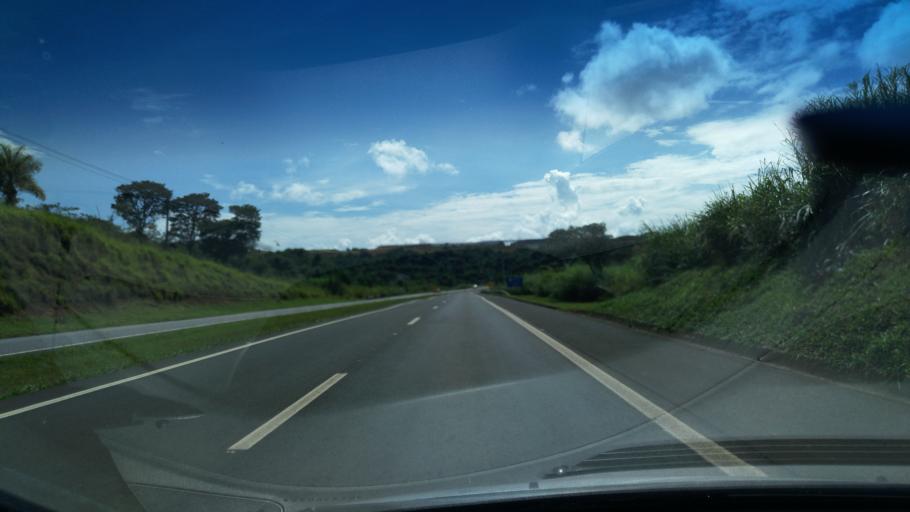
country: BR
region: Sao Paulo
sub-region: Santo Antonio Do Jardim
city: Espirito Santo do Pinhal
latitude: -22.2147
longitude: -46.7853
